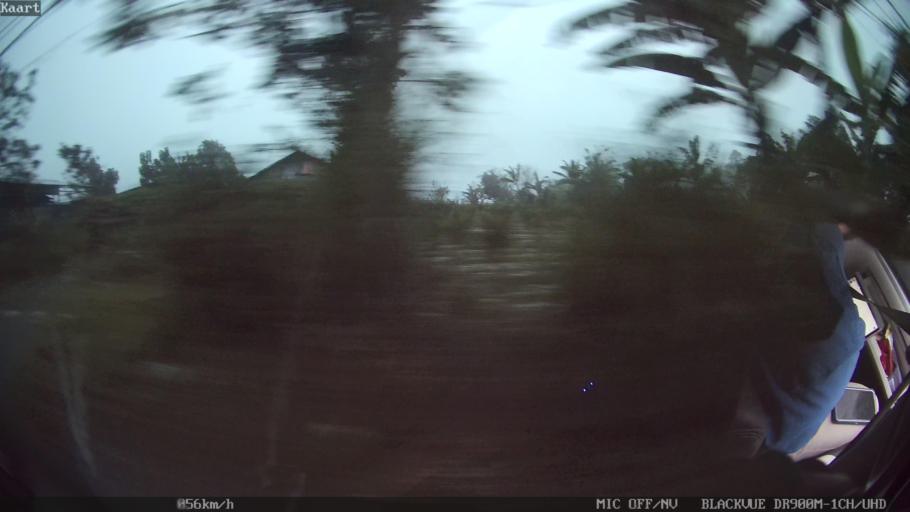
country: ID
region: Bali
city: Banjar Kedisan
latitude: -8.2984
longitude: 115.3107
